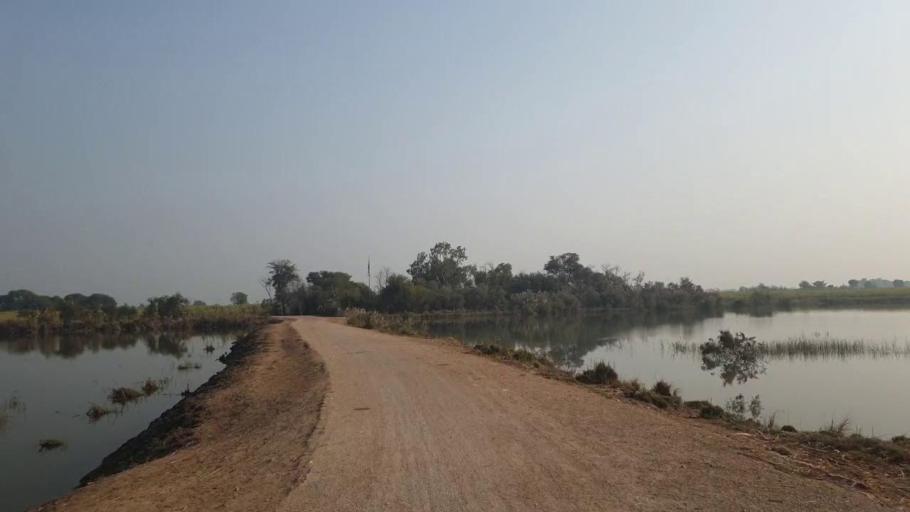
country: PK
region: Sindh
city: Shahdadpur
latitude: 25.9570
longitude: 68.5309
